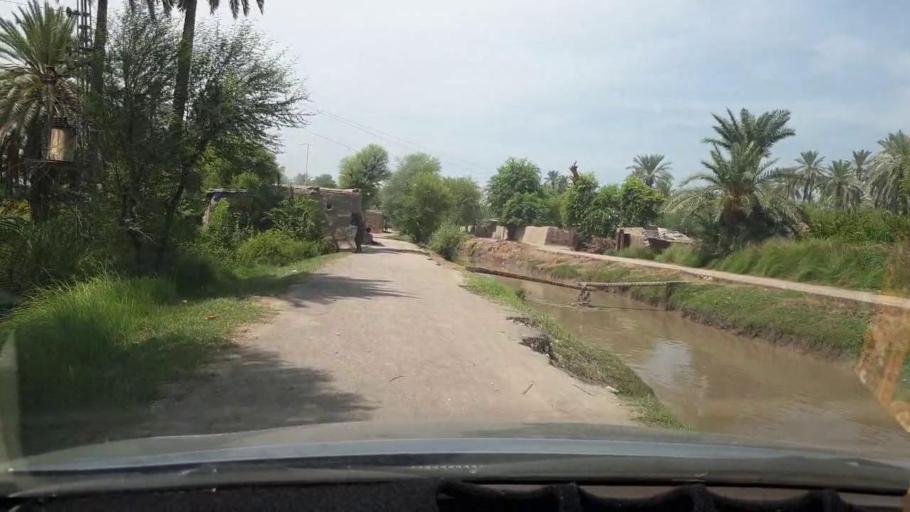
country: PK
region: Sindh
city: Khairpur
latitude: 27.4926
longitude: 68.7433
